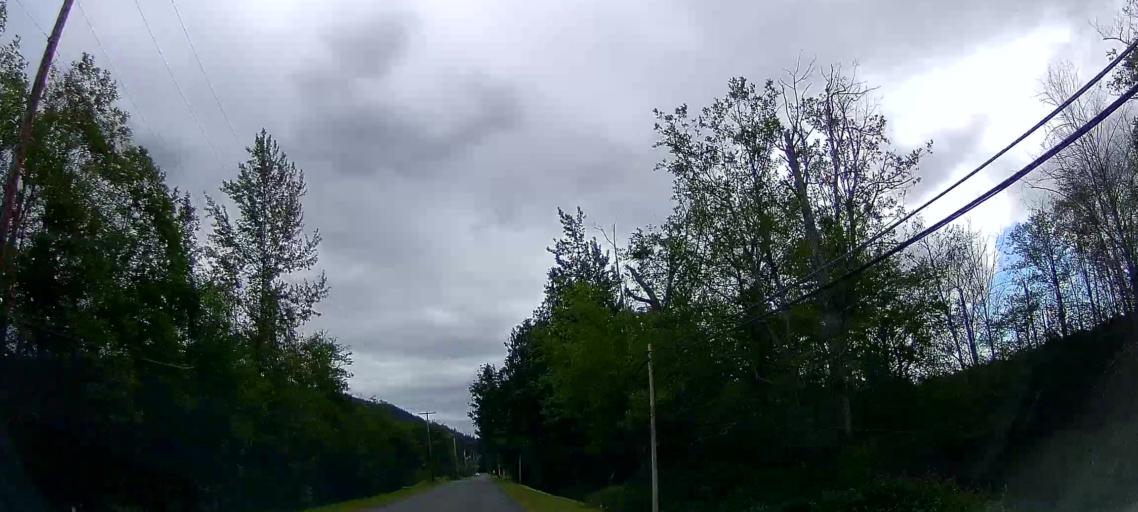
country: US
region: Washington
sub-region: Skagit County
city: Sedro-Woolley
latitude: 48.4954
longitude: -122.2375
